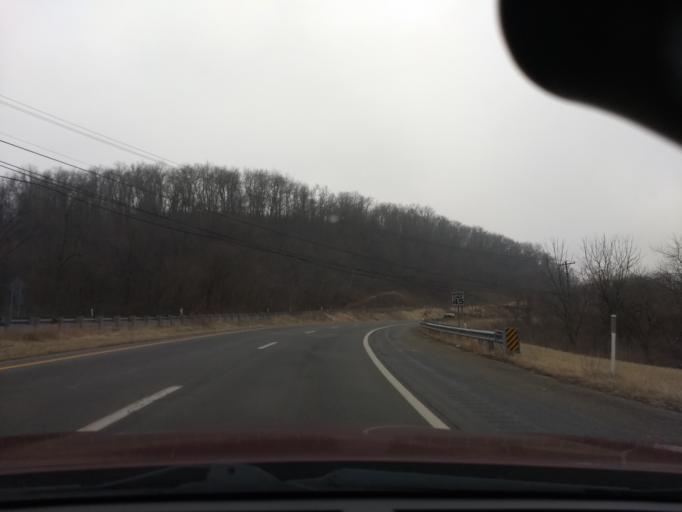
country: US
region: Pennsylvania
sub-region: Allegheny County
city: Turtle Creek
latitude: 40.3941
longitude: -79.8265
